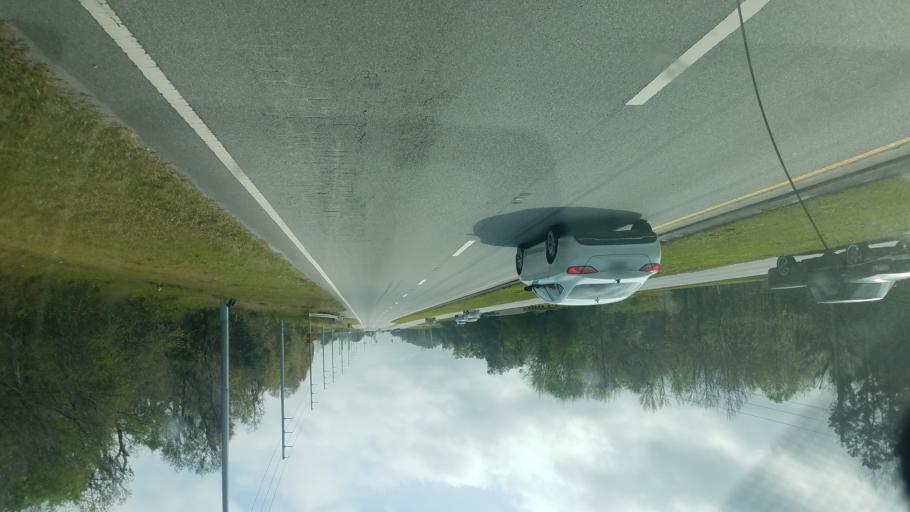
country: US
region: Florida
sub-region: Polk County
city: Winston
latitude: 27.9852
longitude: -82.0560
